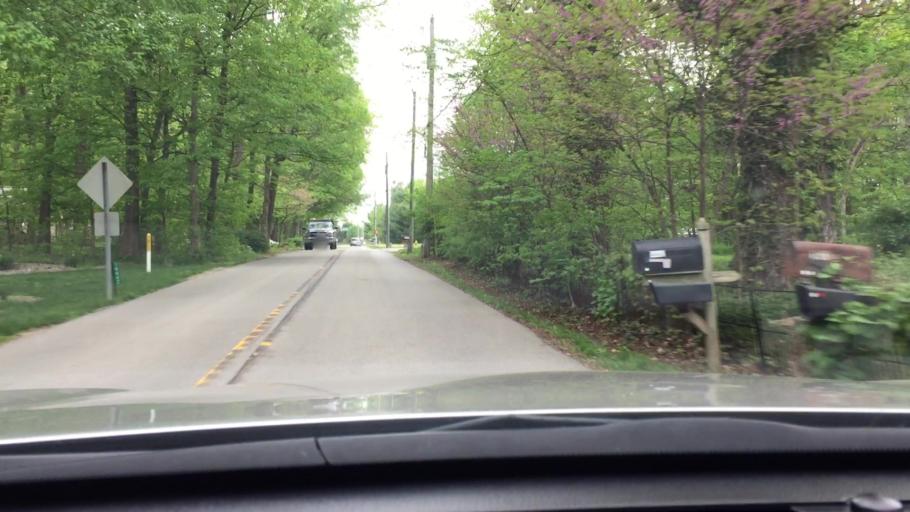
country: US
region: Indiana
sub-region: Hamilton County
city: Carmel
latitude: 39.9980
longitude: -86.0601
